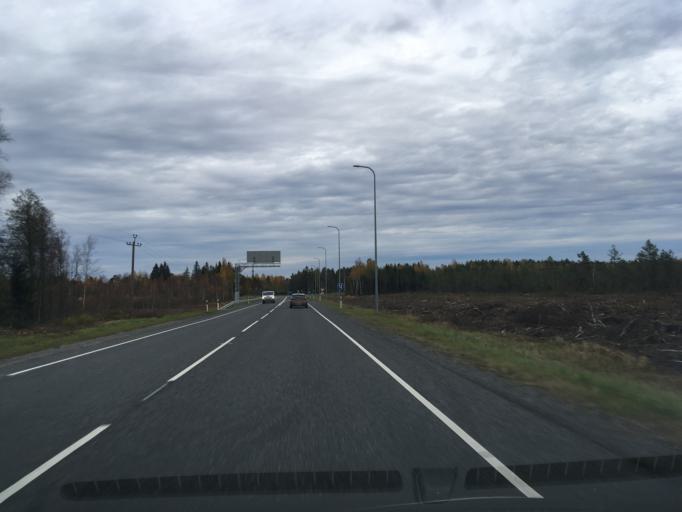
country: EE
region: Harju
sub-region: Nissi vald
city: Turba
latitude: 58.9904
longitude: 24.0583
